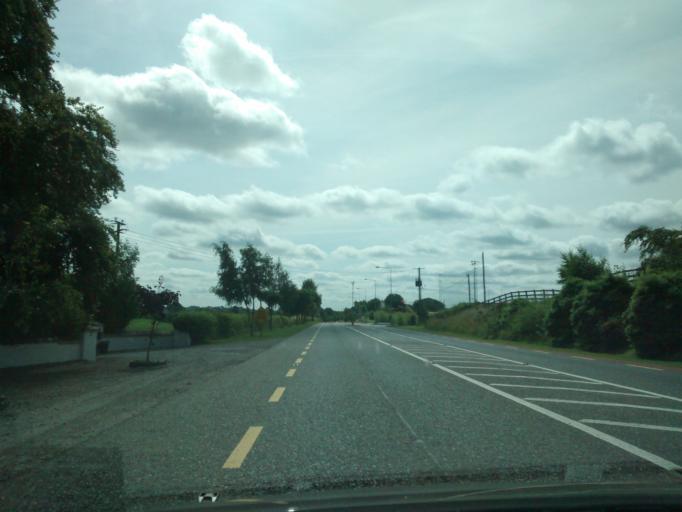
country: IE
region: Leinster
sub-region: Uibh Fhaili
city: Clara
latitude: 53.3753
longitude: -7.6589
